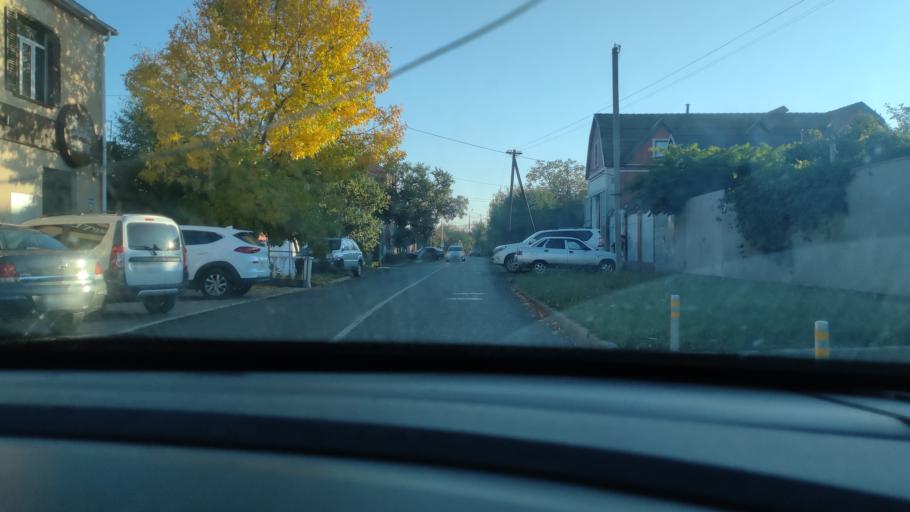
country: RU
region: Krasnodarskiy
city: Krasnodar
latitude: 45.0434
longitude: 38.9344
